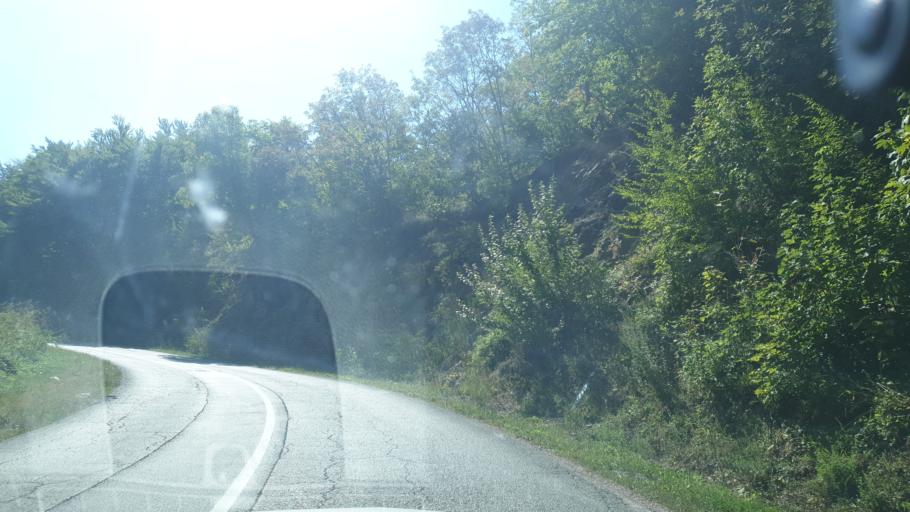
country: RS
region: Central Serbia
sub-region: Kolubarski Okrug
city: Mionica
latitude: 44.1446
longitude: 20.0185
